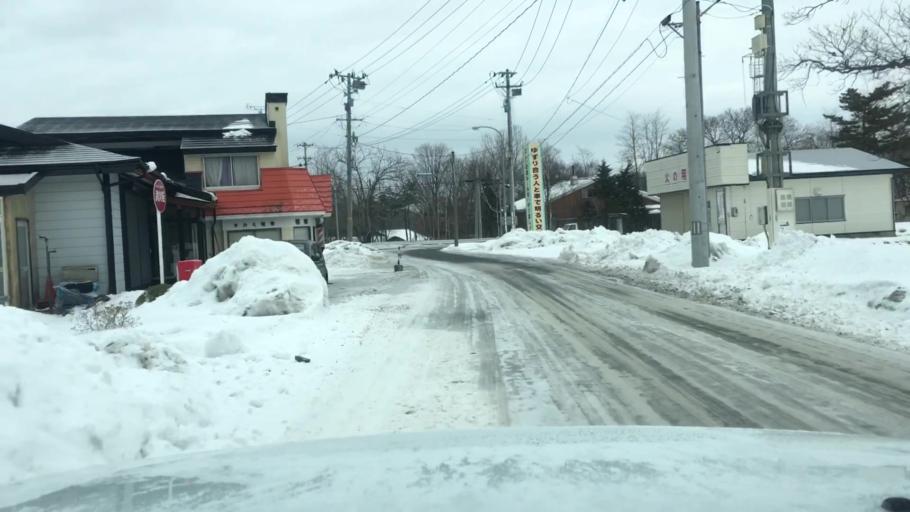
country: JP
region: Iwate
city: Shizukuishi
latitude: 39.9159
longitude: 141.0058
